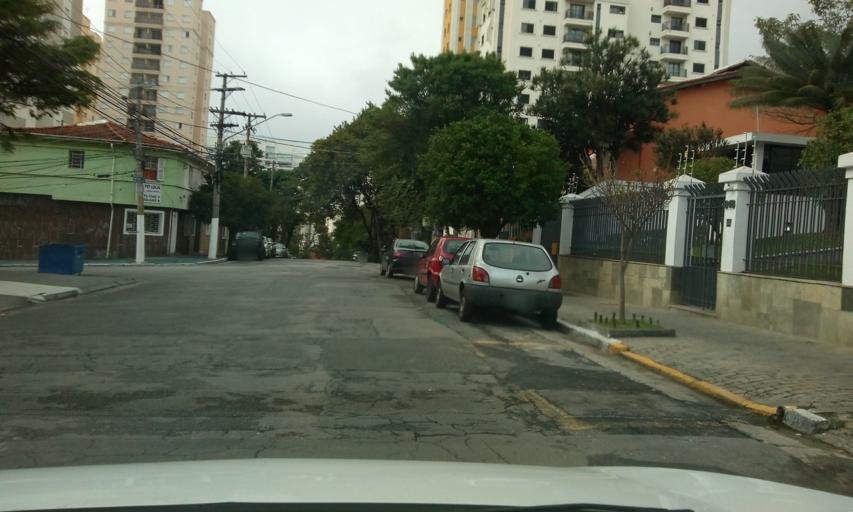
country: BR
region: Sao Paulo
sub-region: Sao Paulo
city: Sao Paulo
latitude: -23.6046
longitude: -46.6303
